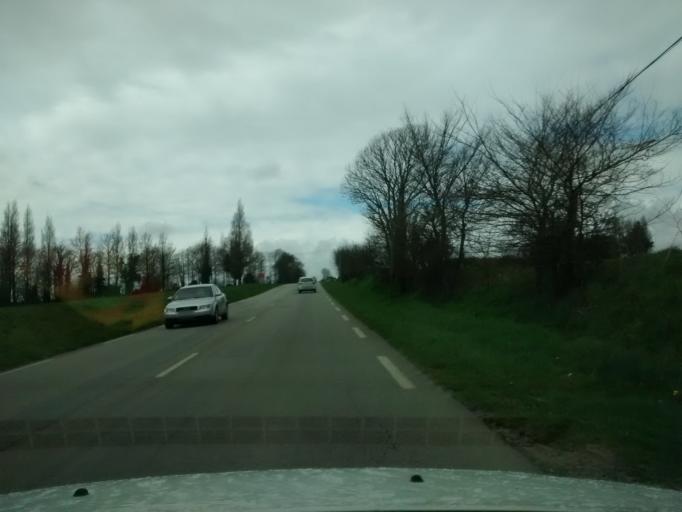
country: FR
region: Brittany
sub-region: Departement du Morbihan
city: Queven
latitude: 47.7711
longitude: -3.4096
